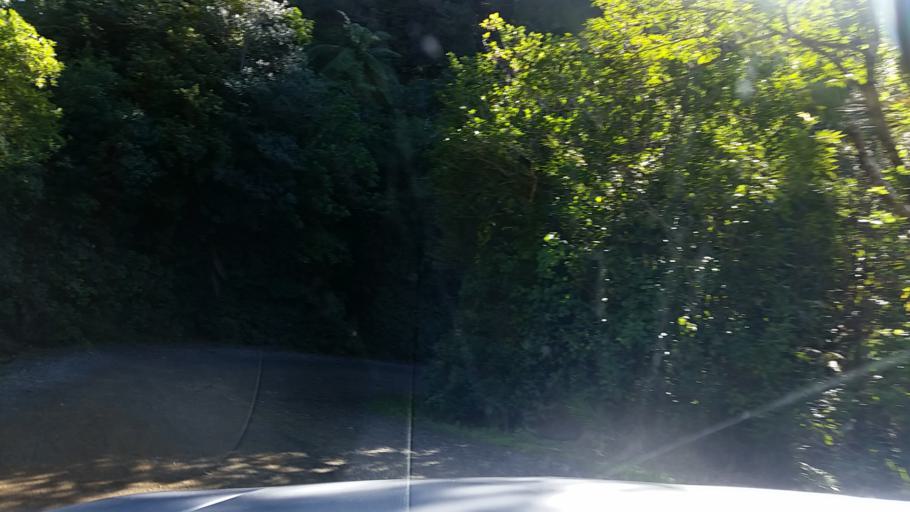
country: NZ
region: Marlborough
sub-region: Marlborough District
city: Picton
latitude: -41.1060
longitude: 173.6536
